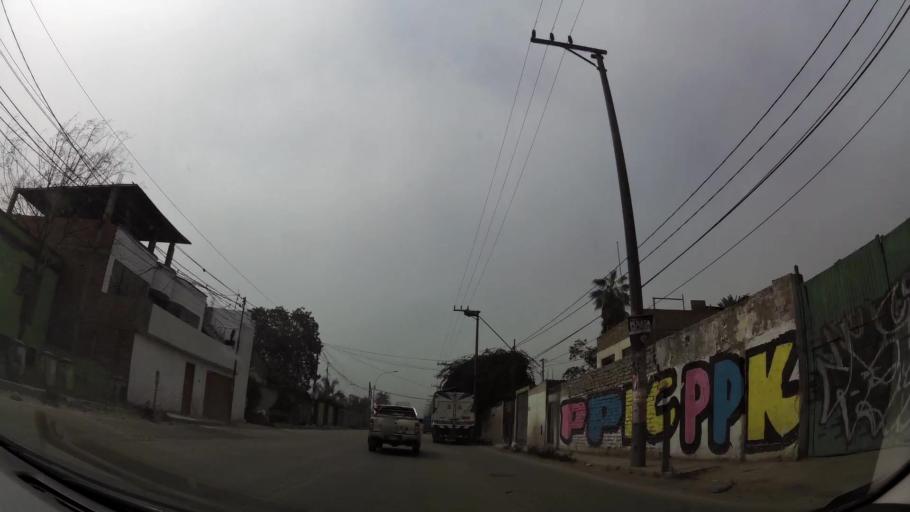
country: PE
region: Lima
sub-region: Lima
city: Chaclacayo
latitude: -11.9703
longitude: -76.7519
